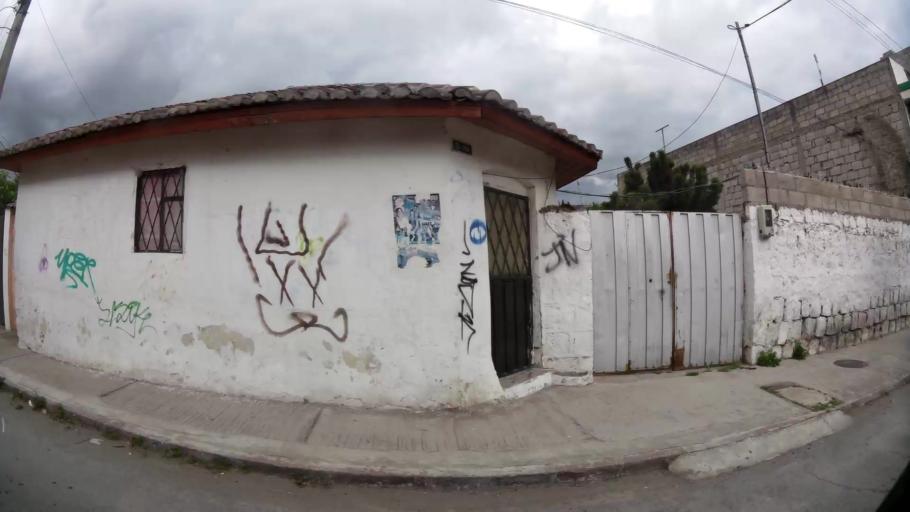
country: EC
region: Pichincha
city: Quito
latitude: -0.0139
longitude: -78.4494
